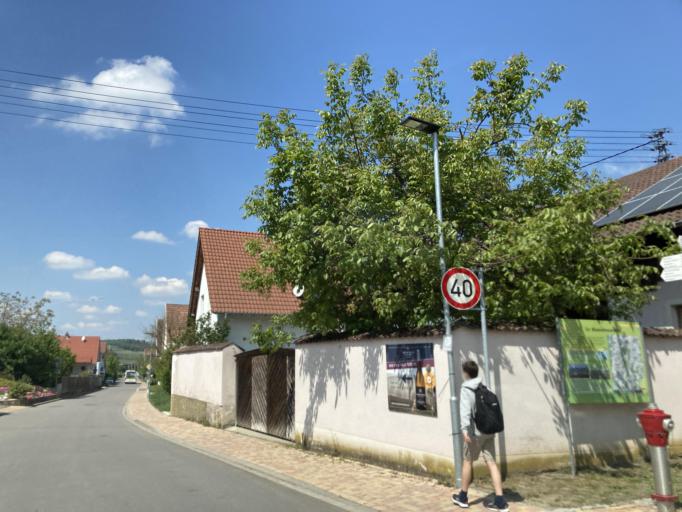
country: DE
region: Baden-Wuerttemberg
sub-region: Freiburg Region
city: Vogtsburg
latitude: 48.1029
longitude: 7.6267
